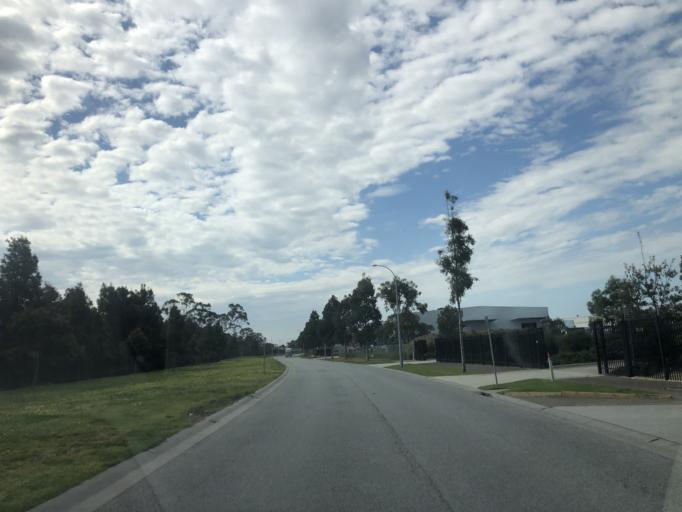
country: AU
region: Victoria
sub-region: Casey
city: Hampton Park
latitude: -38.0373
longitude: 145.2205
